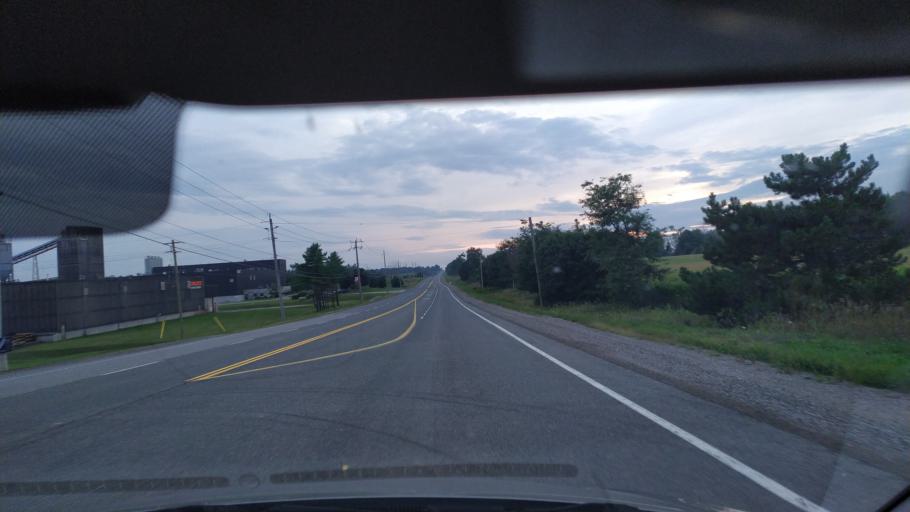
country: CA
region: Ontario
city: Kitchener
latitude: 43.3296
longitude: -80.4583
